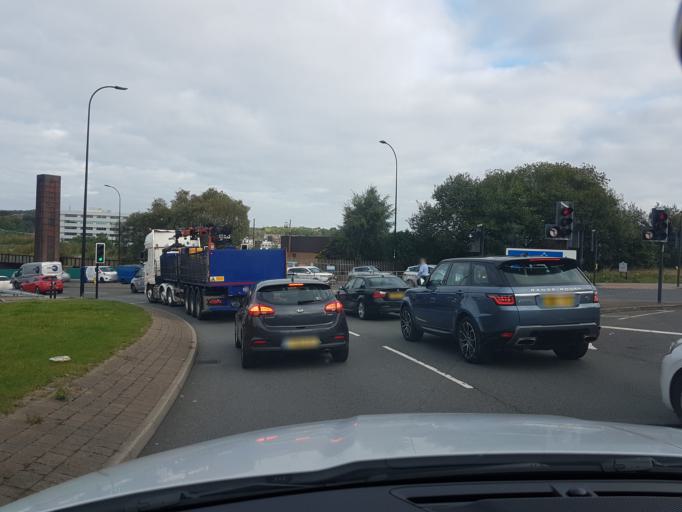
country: GB
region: England
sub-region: Sheffield
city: Sheffield
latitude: 53.3858
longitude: -1.4554
